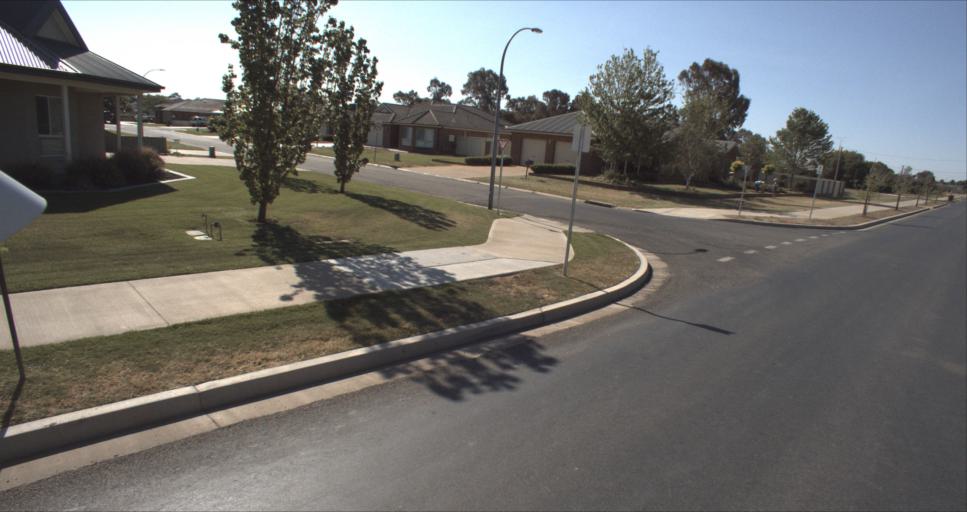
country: AU
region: New South Wales
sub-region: Leeton
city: Leeton
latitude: -34.5529
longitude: 146.4168
